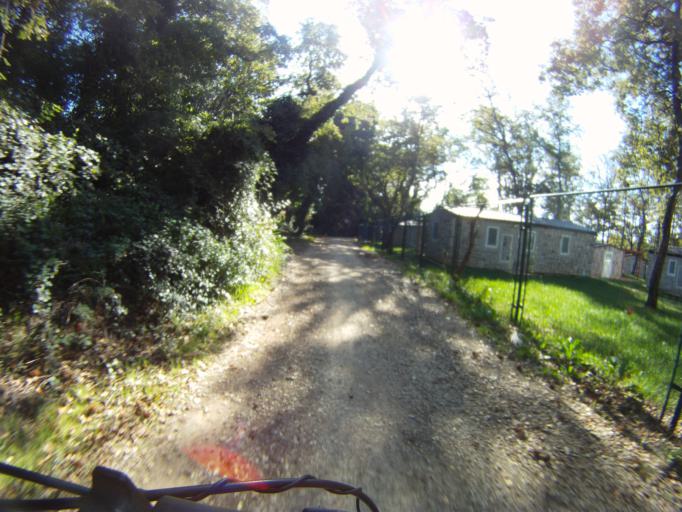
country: HR
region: Istarska
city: Novigrad
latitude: 45.3414
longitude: 13.5509
